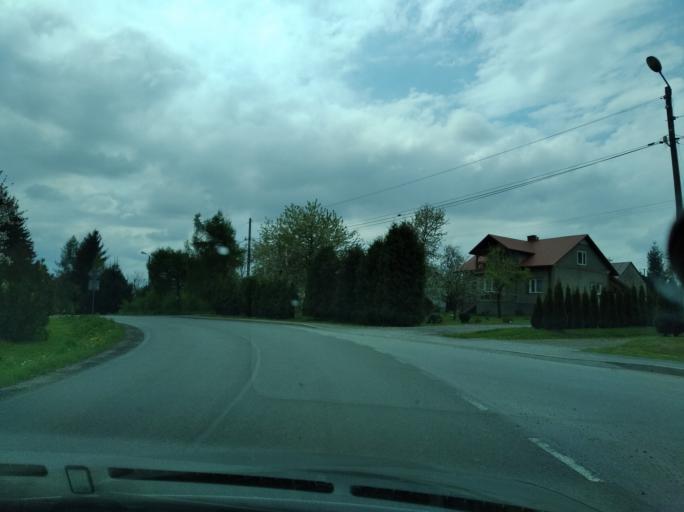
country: PL
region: Subcarpathian Voivodeship
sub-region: Powiat brzozowski
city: Jasionow
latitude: 49.6515
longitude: 21.9772
